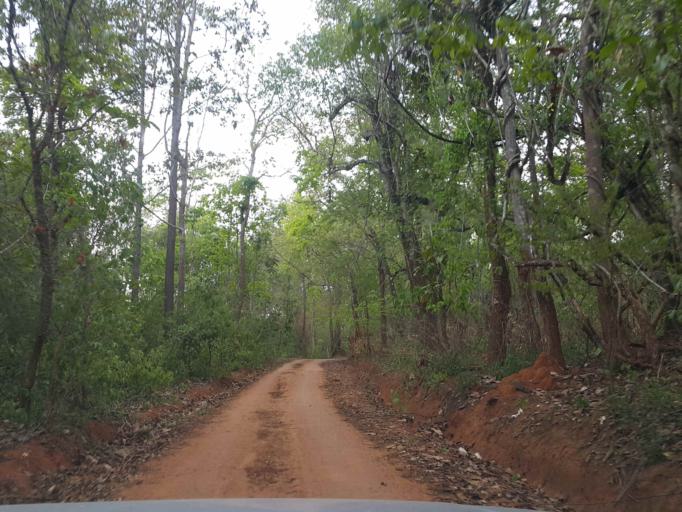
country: TH
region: Chiang Mai
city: Wiang Haeng
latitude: 19.3685
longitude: 98.7183
